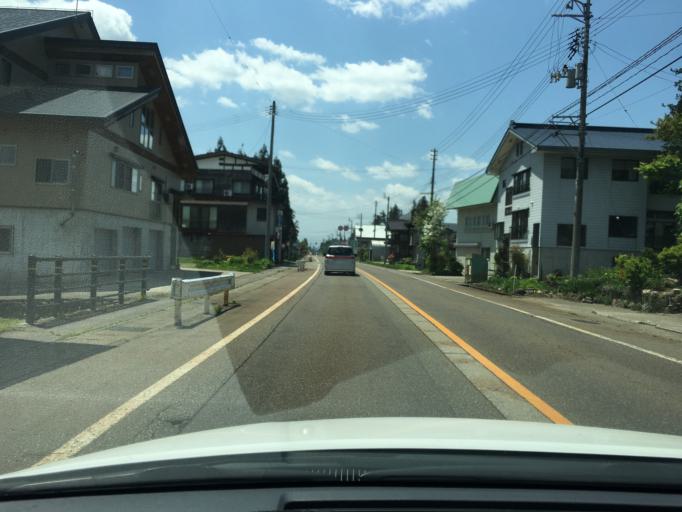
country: JP
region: Niigata
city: Tochio-honcho
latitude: 37.2927
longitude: 138.9903
